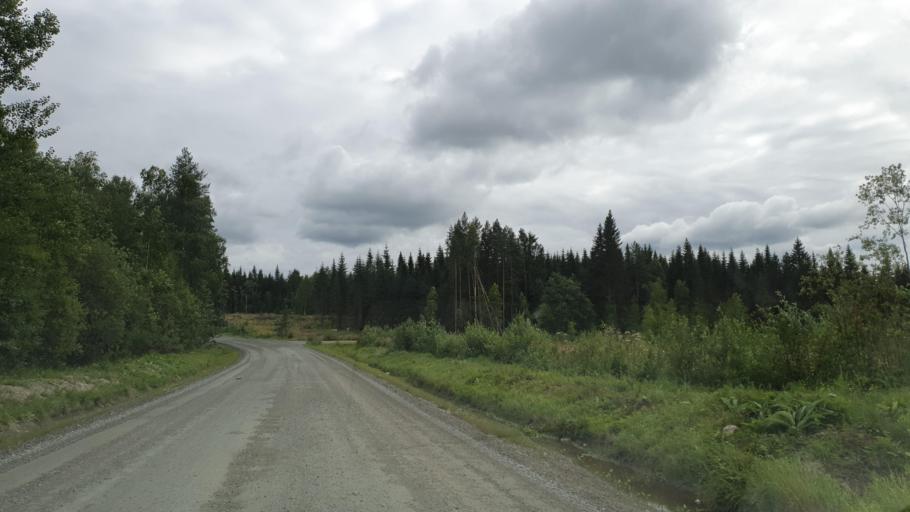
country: FI
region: Northern Savo
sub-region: Ylae-Savo
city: Iisalmi
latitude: 63.5278
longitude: 27.0888
